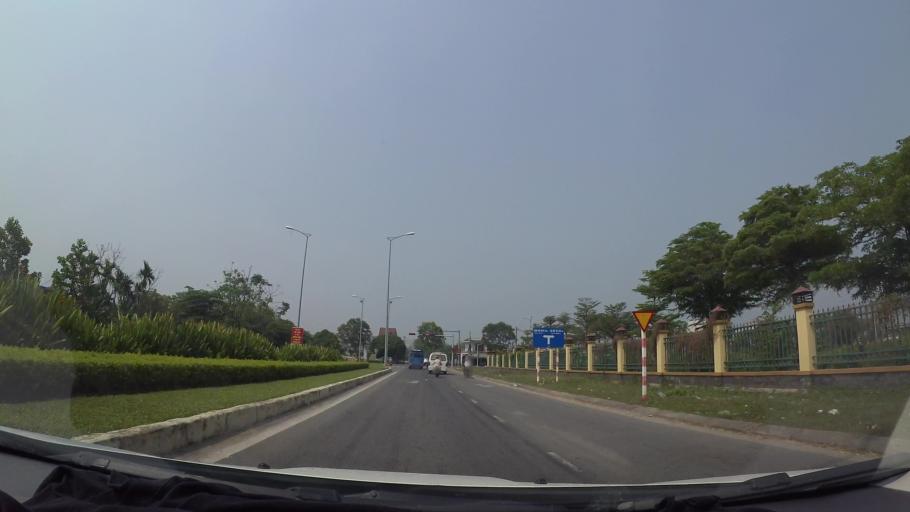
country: VN
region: Da Nang
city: Cam Le
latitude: 15.9669
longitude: 108.2119
